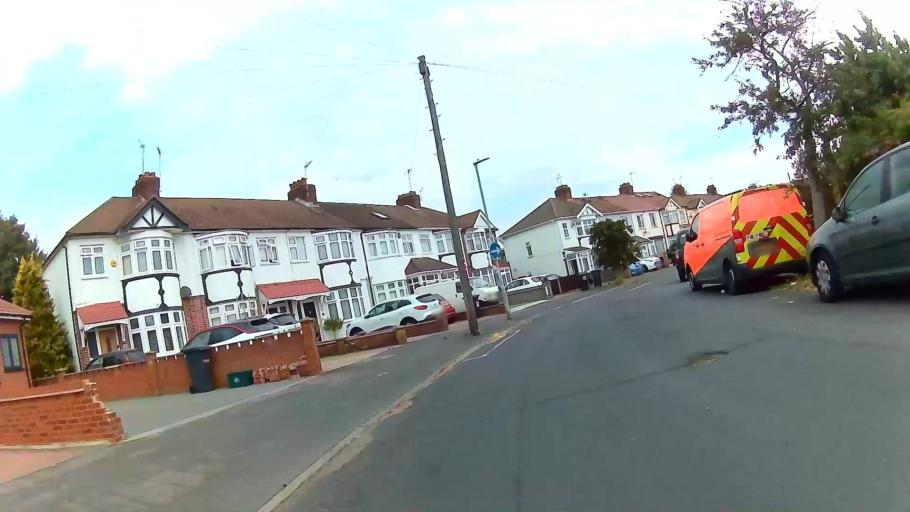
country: GB
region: England
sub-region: Hertfordshire
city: Waltham Cross
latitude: 51.6835
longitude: -0.0364
